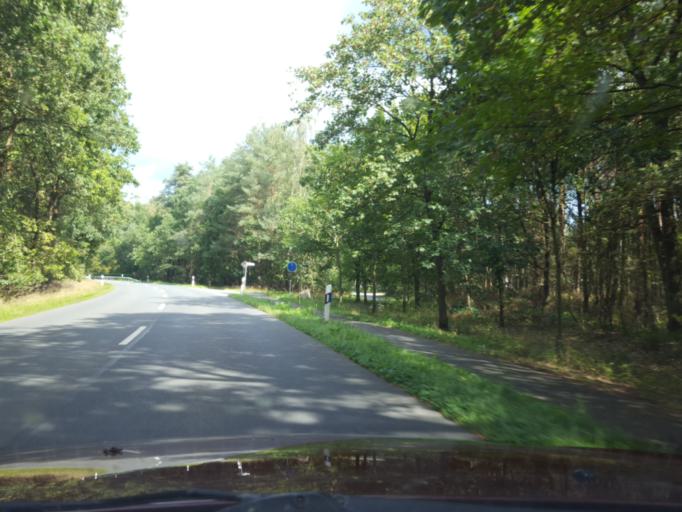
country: DE
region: Lower Saxony
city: Hemsbunde
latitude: 53.0732
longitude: 9.4516
